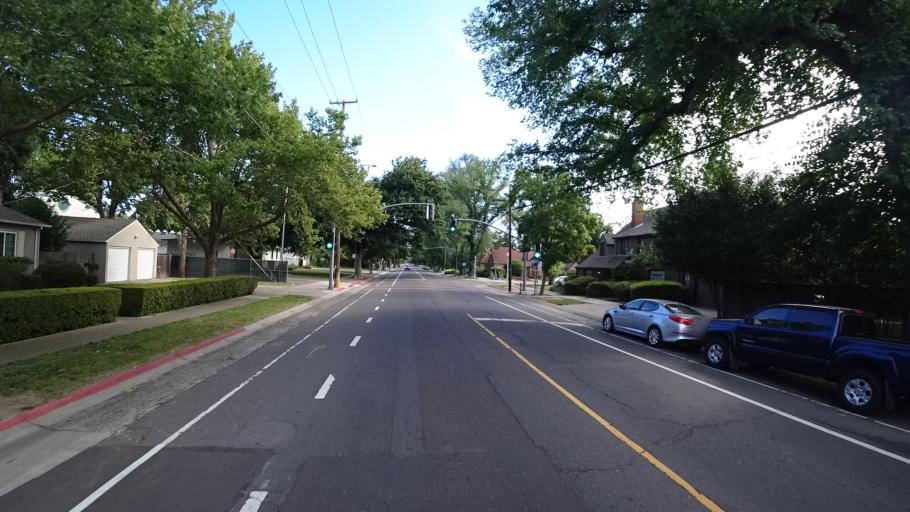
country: US
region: California
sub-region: Sacramento County
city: Sacramento
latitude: 38.5521
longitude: -121.5047
